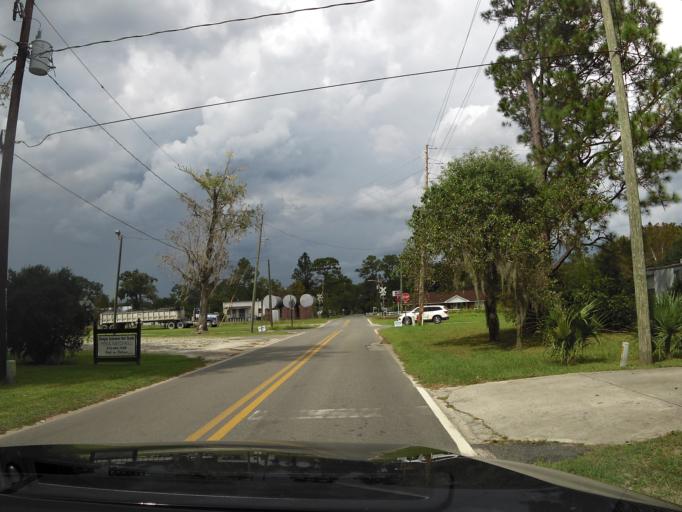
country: US
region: Georgia
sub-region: Brantley County
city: Nahunta
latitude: 31.2040
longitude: -81.9796
